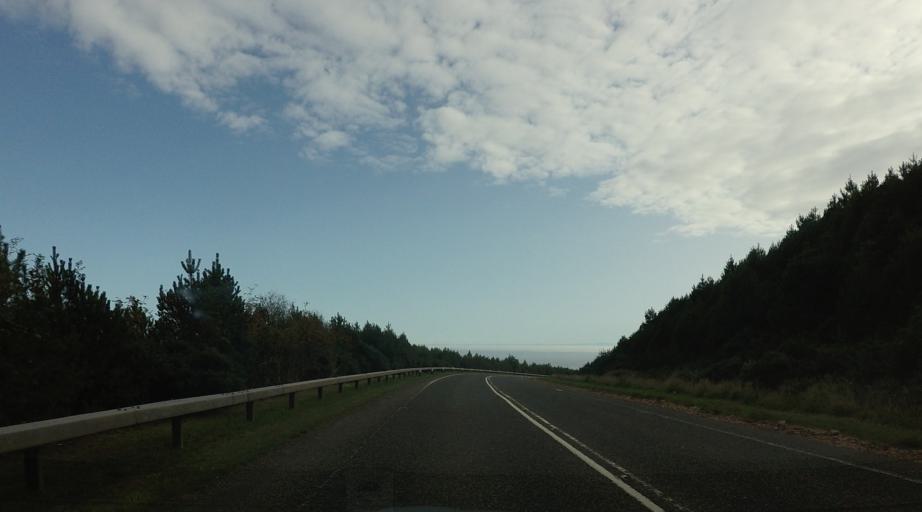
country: GB
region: Scotland
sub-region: Highland
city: Brora
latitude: 58.1398
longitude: -3.6100
